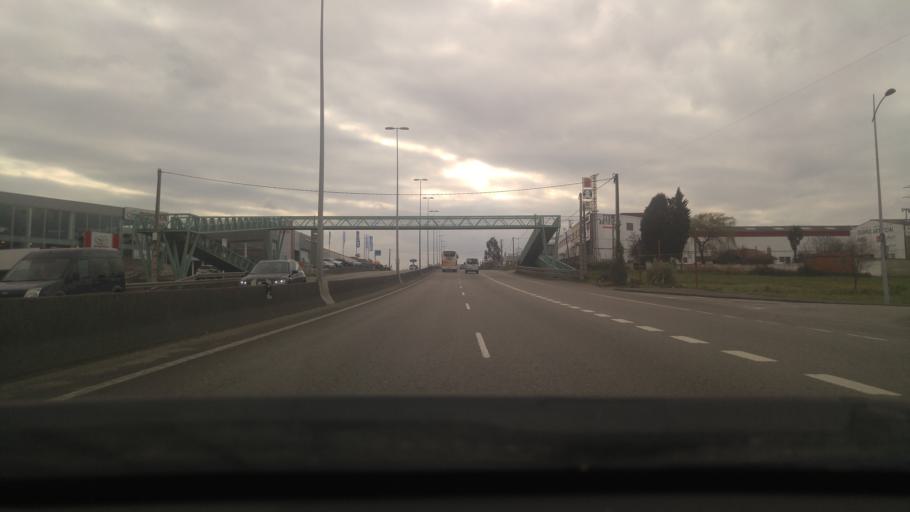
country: ES
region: Asturias
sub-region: Province of Asturias
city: Natahoyo
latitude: 43.5073
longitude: -5.6961
